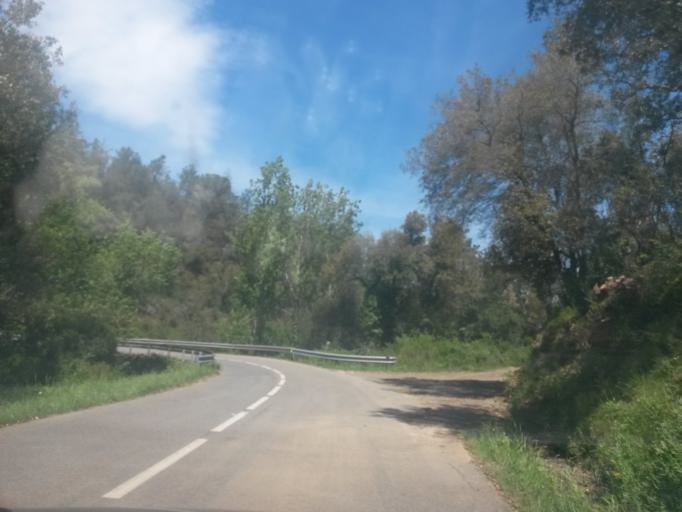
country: ES
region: Catalonia
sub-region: Provincia de Girona
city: Madremanya
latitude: 41.9386
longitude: 2.9495
